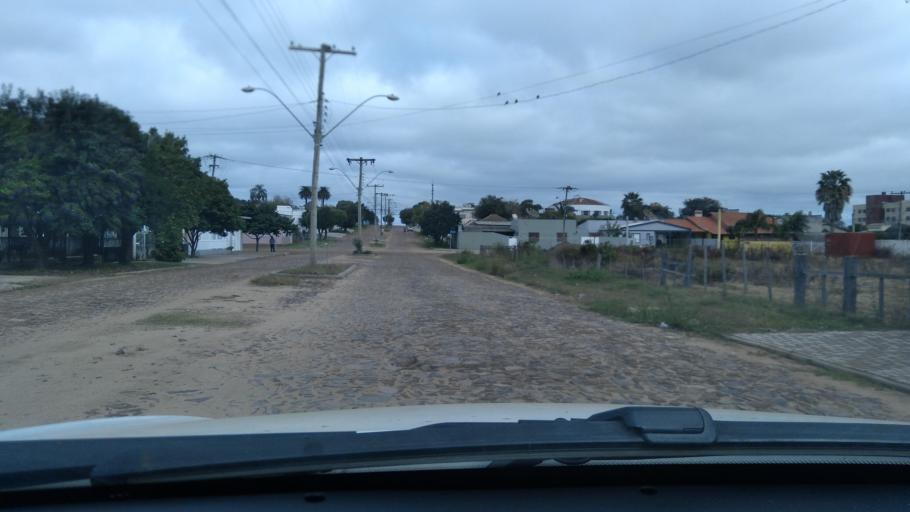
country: BR
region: Rio Grande do Sul
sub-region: Dom Pedrito
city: Dom Pedrito
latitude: -30.9838
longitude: -54.6629
